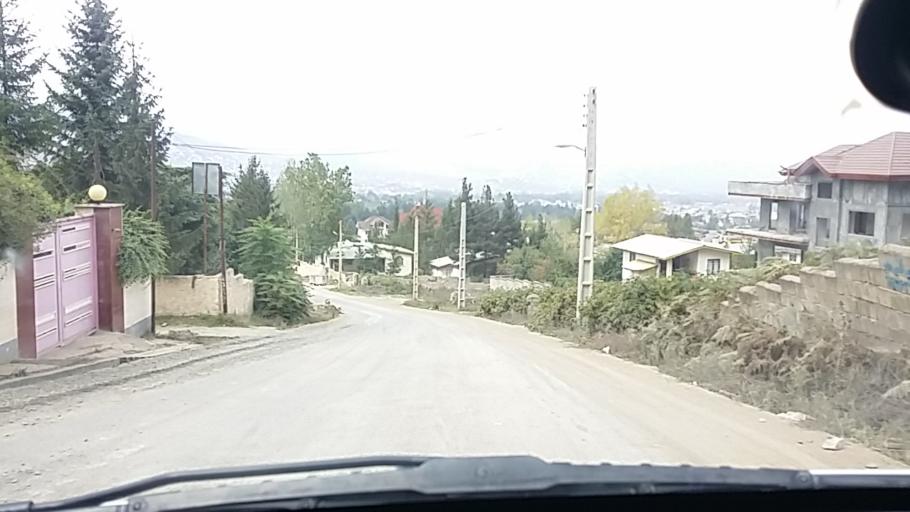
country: IR
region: Mazandaran
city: `Abbasabad
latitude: 36.4944
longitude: 51.1654
